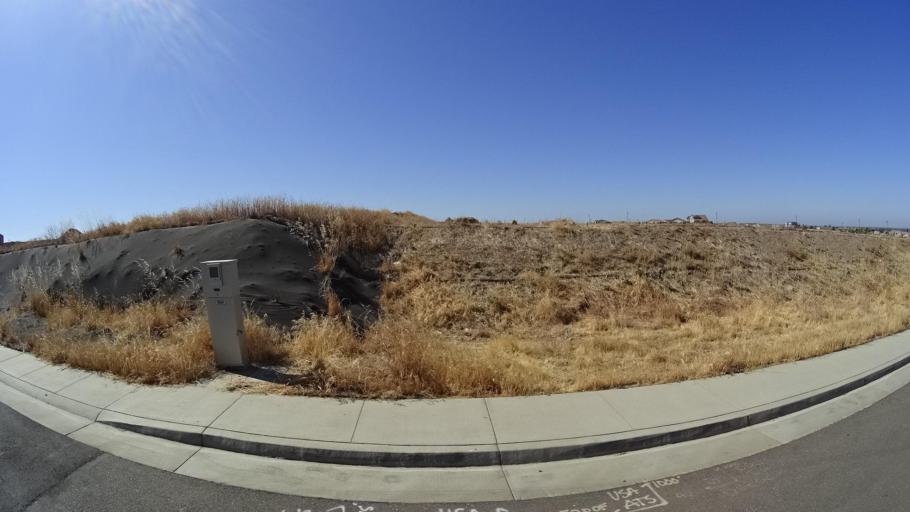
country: US
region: California
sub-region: Placer County
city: Rocklin
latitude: 38.8358
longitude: -121.2667
